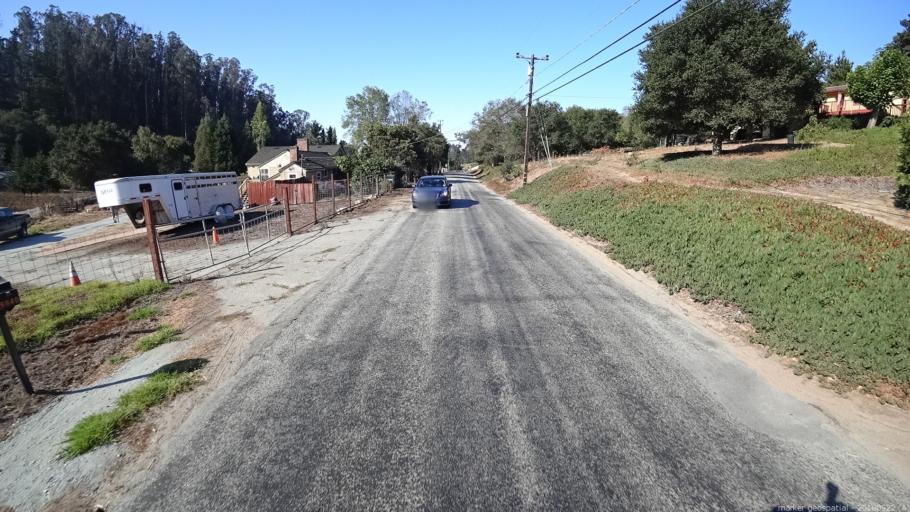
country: US
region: California
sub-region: Monterey County
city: Prunedale
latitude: 36.8215
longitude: -121.6444
